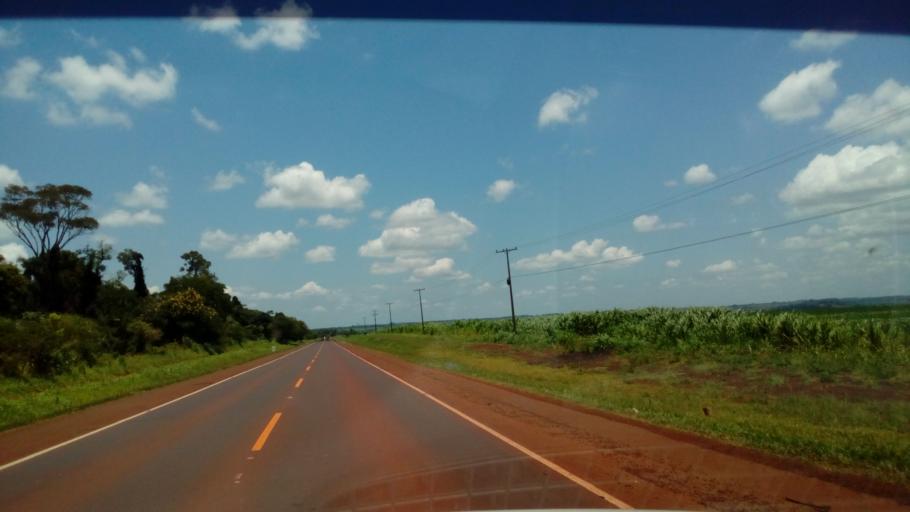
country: PY
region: Itapua
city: Arquitecto Tomas Romero Pereira
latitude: -26.3931
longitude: -55.2297
